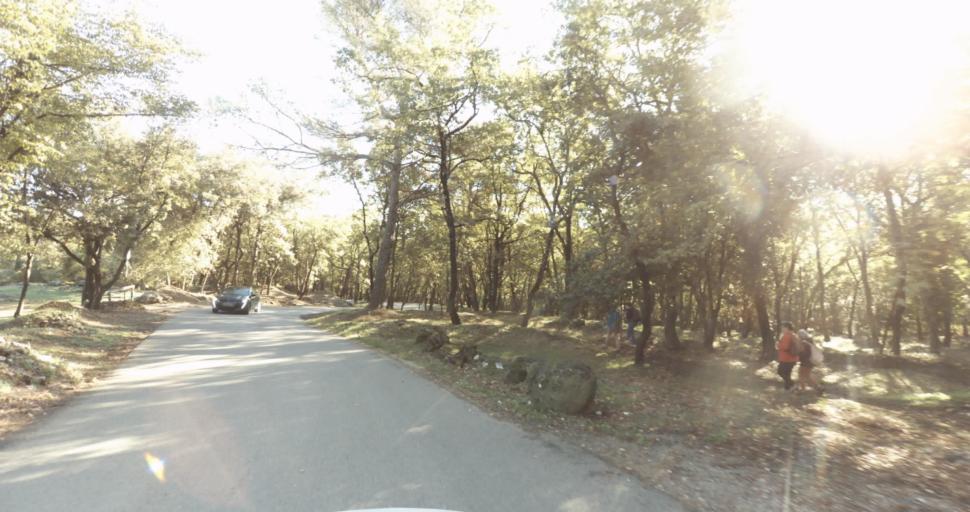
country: FR
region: Provence-Alpes-Cote d'Azur
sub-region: Departement des Alpes-Maritimes
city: Vence
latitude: 43.7128
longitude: 7.0970
